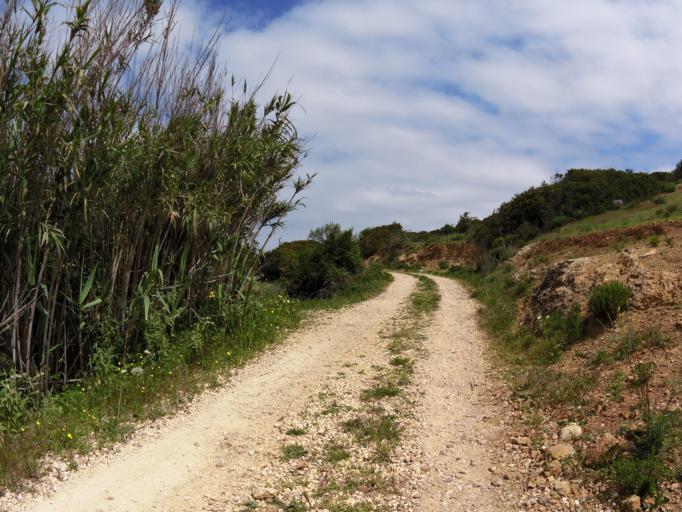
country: PT
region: Faro
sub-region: Vila do Bispo
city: Vila do Bispo
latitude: 37.0686
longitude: -8.8721
